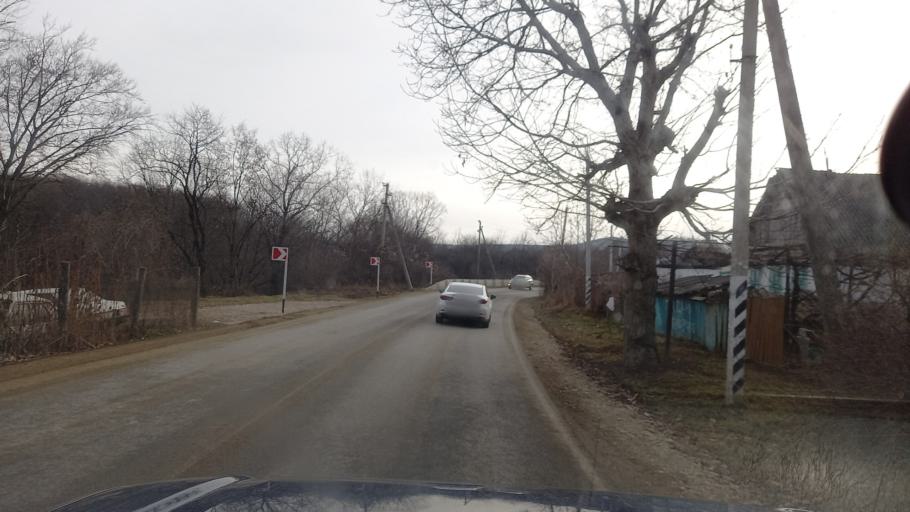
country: RU
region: Adygeya
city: Kamennomostskiy
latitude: 44.2967
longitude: 40.1902
